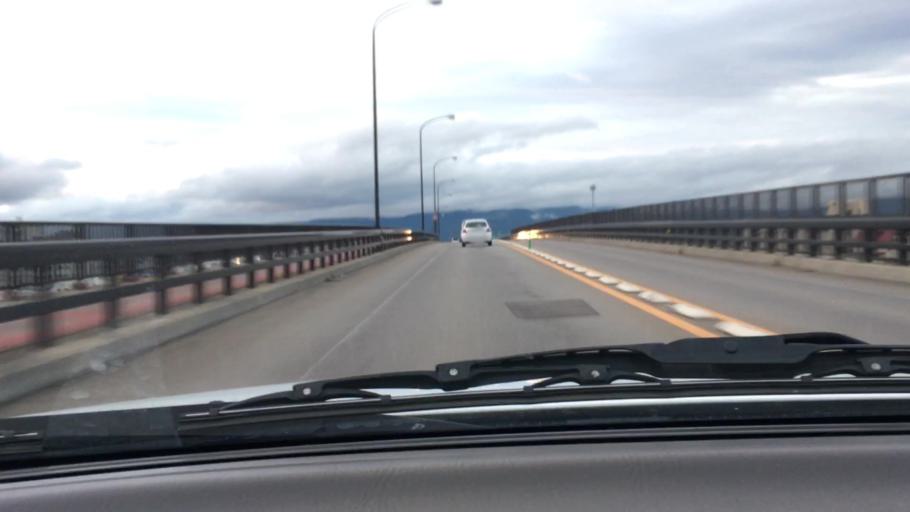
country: JP
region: Hokkaido
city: Hakodate
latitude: 41.7792
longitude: 140.7261
